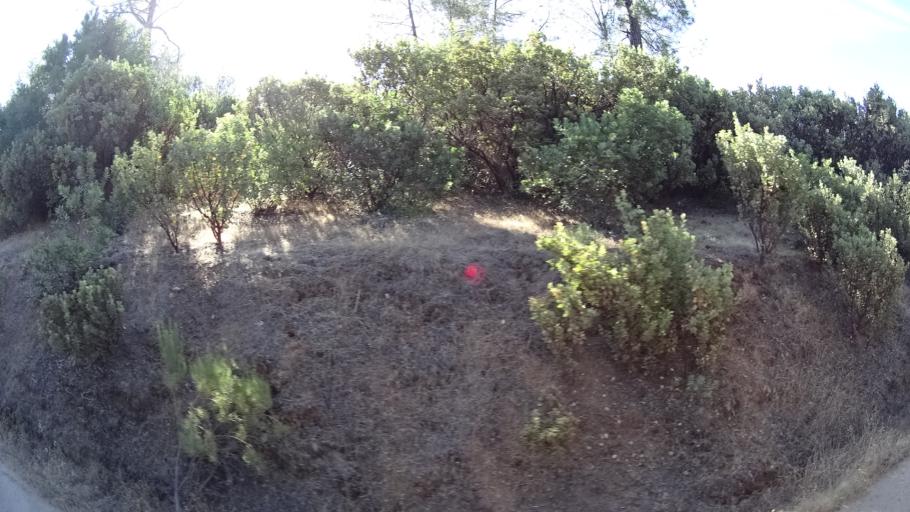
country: US
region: California
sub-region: Calaveras County
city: Mountain Ranch
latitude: 38.1761
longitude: -120.5255
